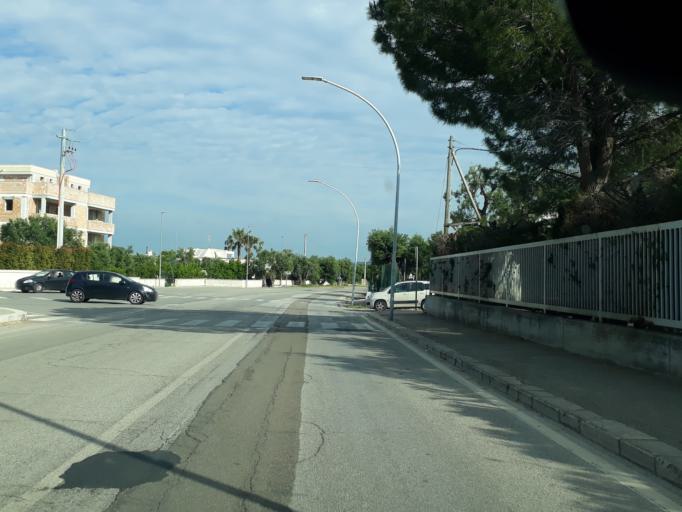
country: IT
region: Apulia
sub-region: Provincia di Brindisi
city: Fasano
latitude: 40.8299
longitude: 17.3657
